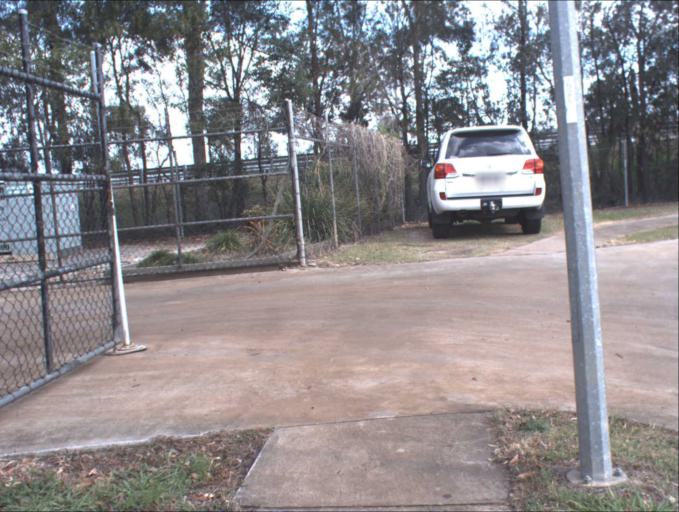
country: AU
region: Queensland
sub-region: Logan
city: Slacks Creek
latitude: -27.6656
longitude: 153.1330
